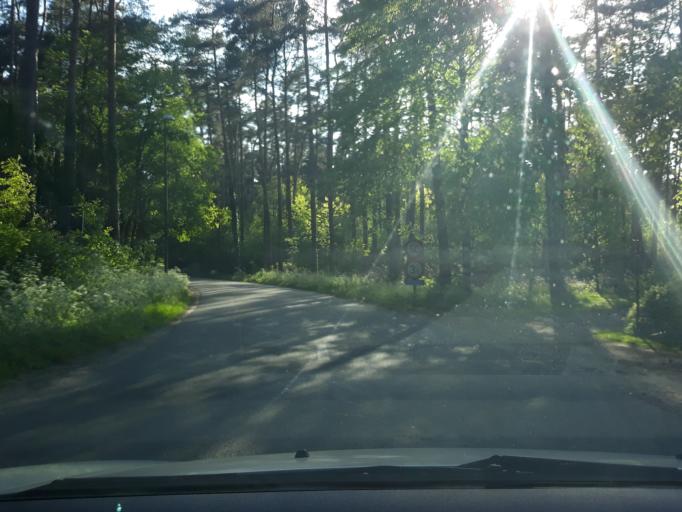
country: BE
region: Flanders
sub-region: Provincie Antwerpen
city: Grobbendonk
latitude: 51.2075
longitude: 4.7501
